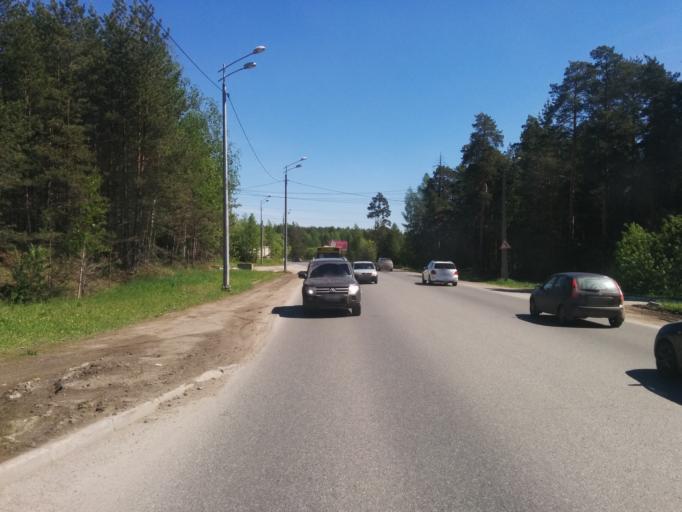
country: RU
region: Perm
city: Kondratovo
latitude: 58.0355
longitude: 56.1497
